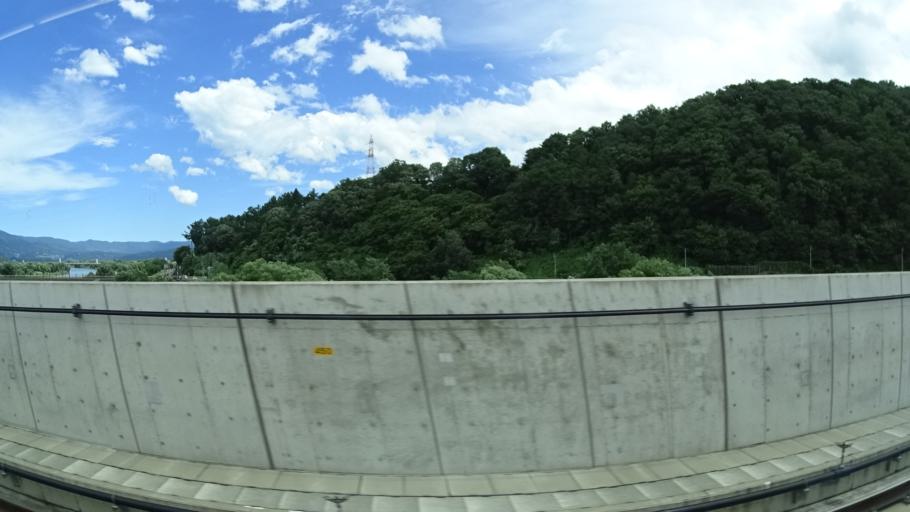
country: JP
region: Nagano
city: Iiyama
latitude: 36.8434
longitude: 138.3605
